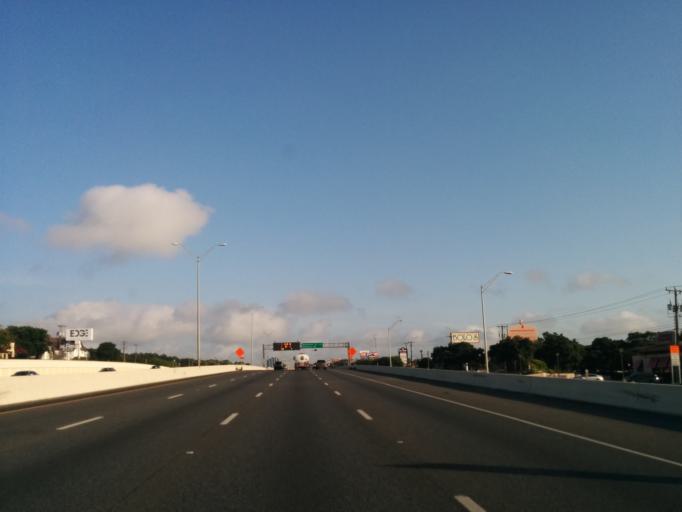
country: US
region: Texas
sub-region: Bexar County
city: Balcones Heights
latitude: 29.5333
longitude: -98.5642
